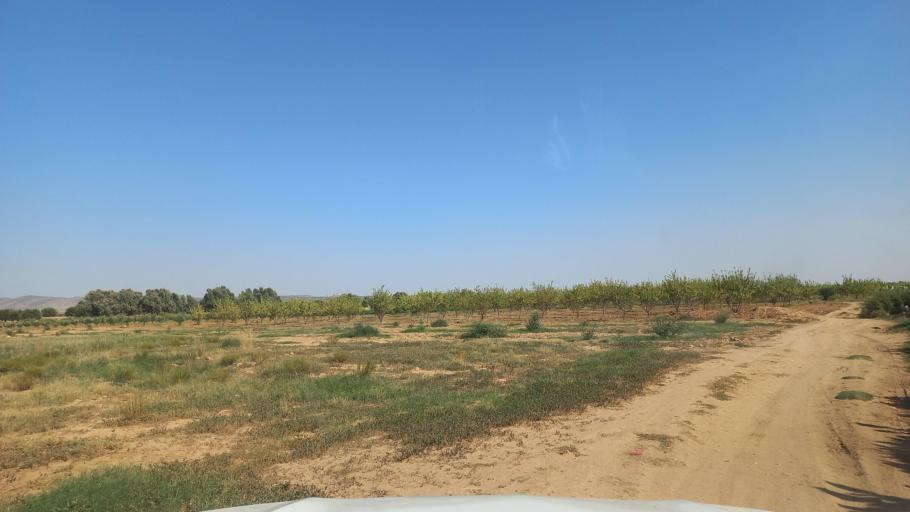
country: TN
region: Al Qasrayn
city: Sbiba
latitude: 35.3052
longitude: 9.0413
